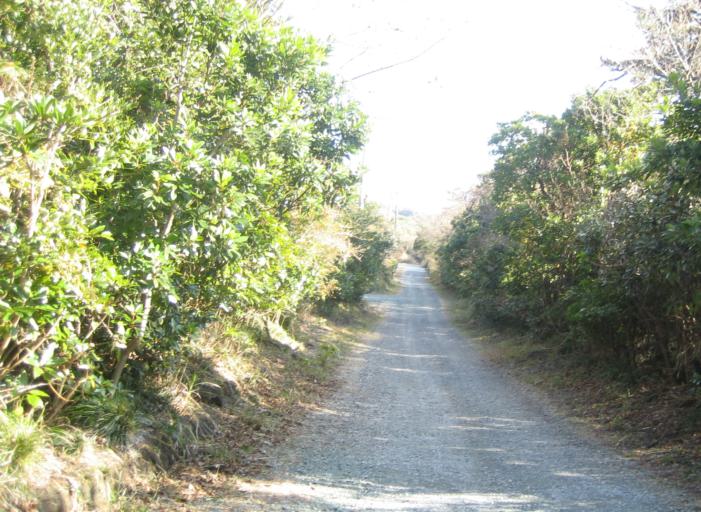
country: JP
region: Shizuoka
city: Ito
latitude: 34.7023
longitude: 139.3708
